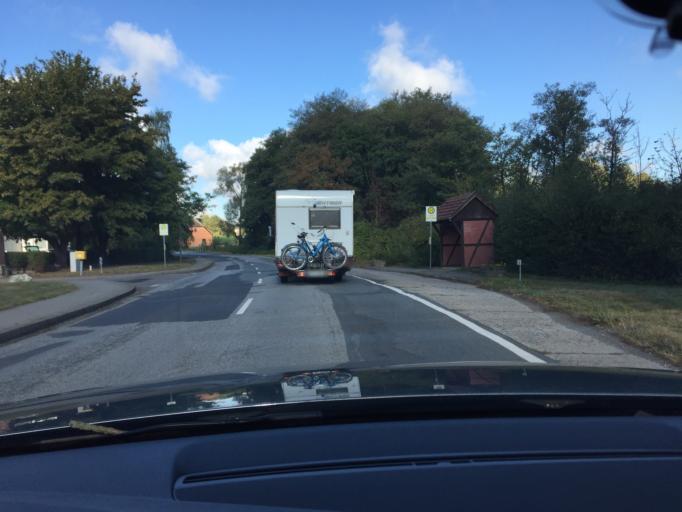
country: DE
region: Mecklenburg-Vorpommern
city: Lalendorf
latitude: 53.6836
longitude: 12.3610
